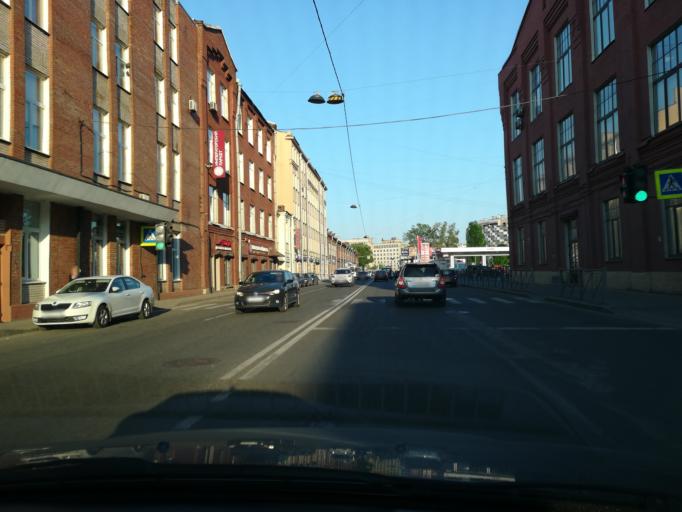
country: RU
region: St.-Petersburg
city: Vasyl'evsky Ostrov
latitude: 59.9538
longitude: 30.2593
